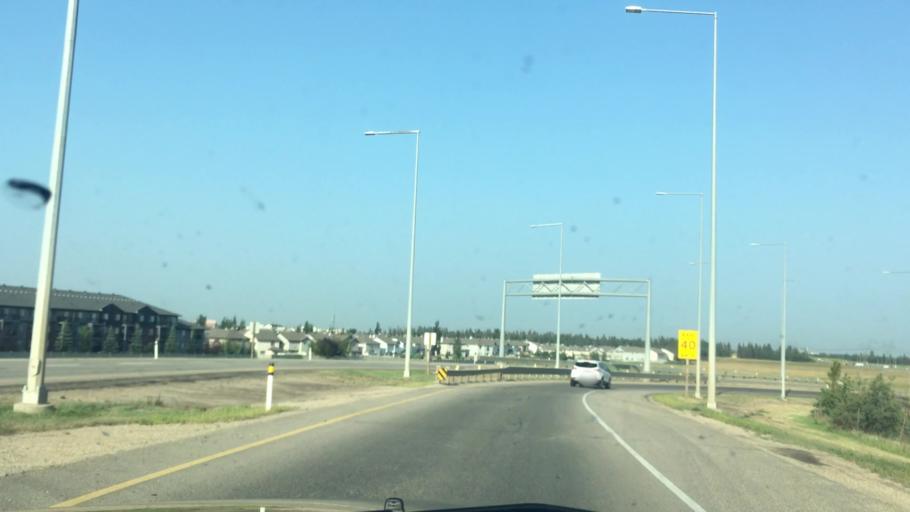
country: CA
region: Alberta
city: Edmonton
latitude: 53.4332
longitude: -113.5203
